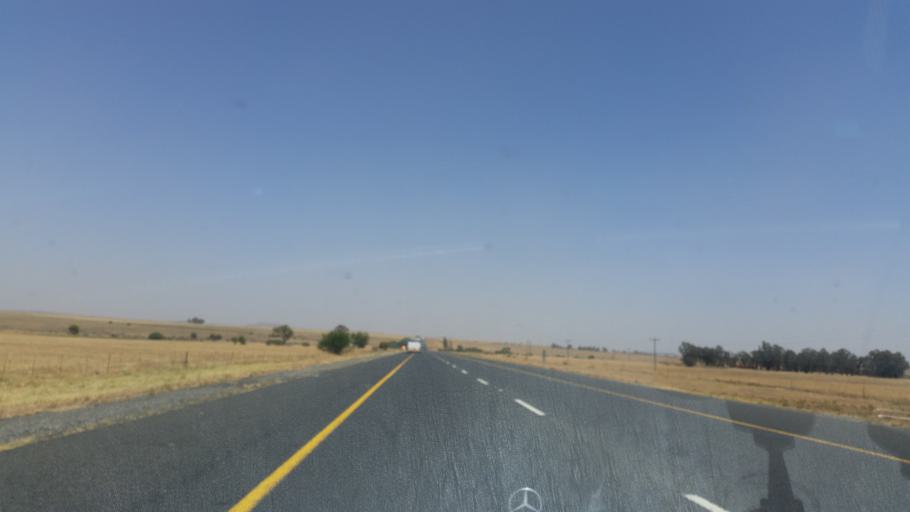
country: ZA
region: Orange Free State
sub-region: Lejweleputswa District Municipality
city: Brandfort
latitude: -28.7279
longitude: 26.7649
